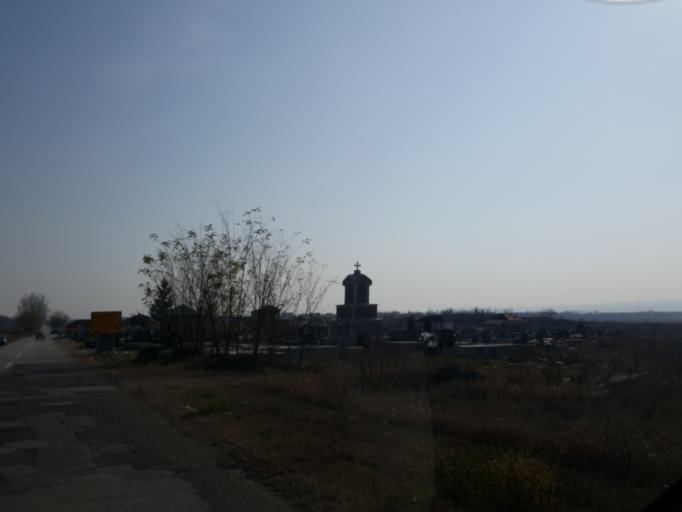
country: RS
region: Central Serbia
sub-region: Borski Okrug
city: Negotin
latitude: 44.2095
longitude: 22.5832
